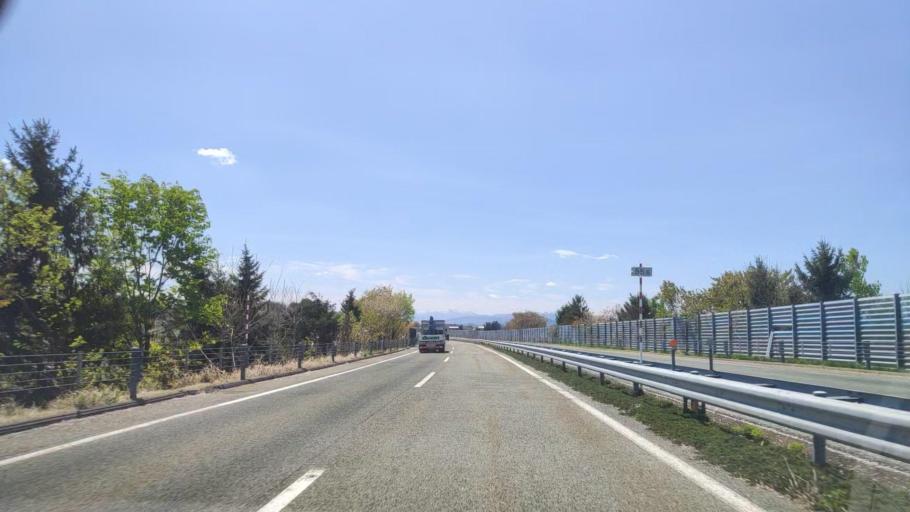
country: JP
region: Akita
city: Yokotemachi
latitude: 39.3138
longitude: 140.5158
